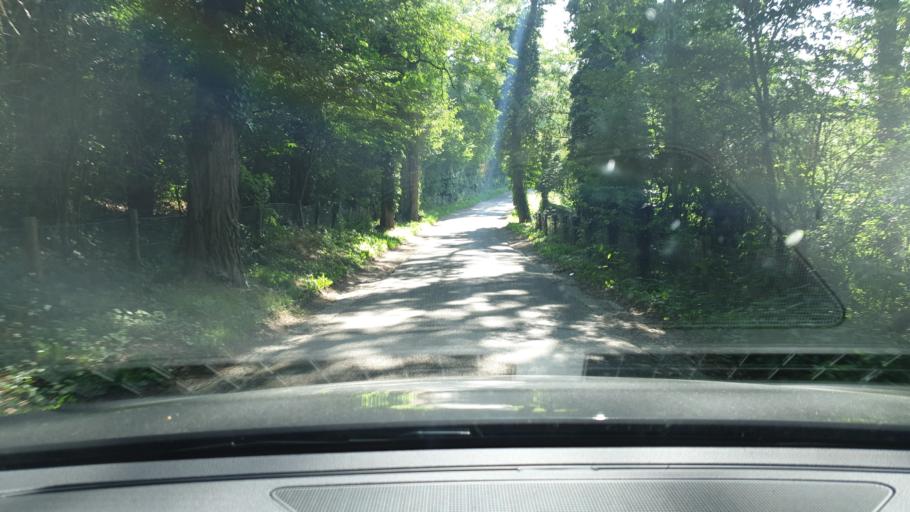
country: NL
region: Limburg
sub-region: Eijsden-Margraten
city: Margraten
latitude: 50.8212
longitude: 5.7890
